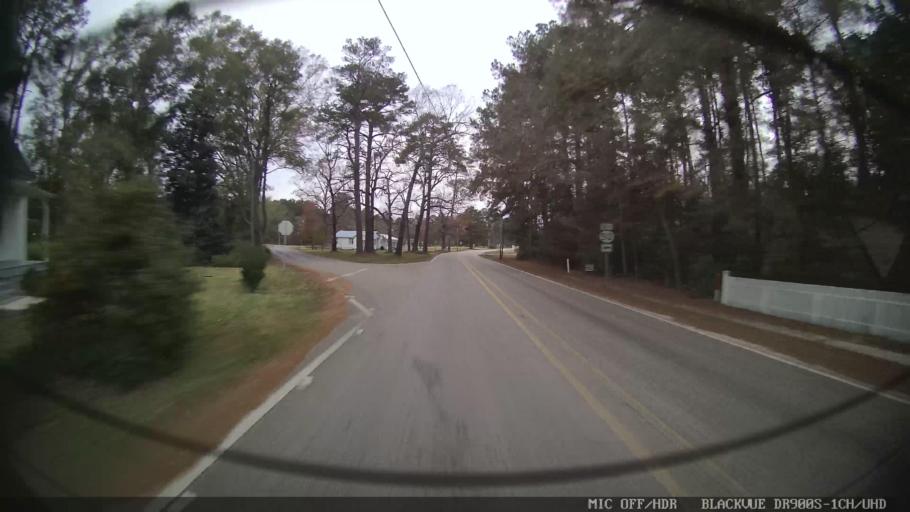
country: US
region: Mississippi
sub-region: Clarke County
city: Stonewall
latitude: 32.0410
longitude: -88.8873
